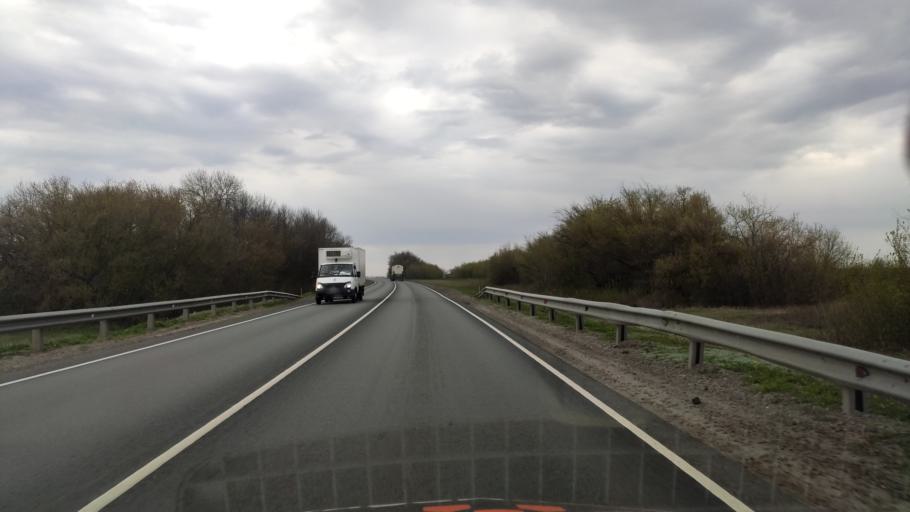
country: RU
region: Voronezj
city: Nizhnedevitsk
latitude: 51.6125
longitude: 38.6152
